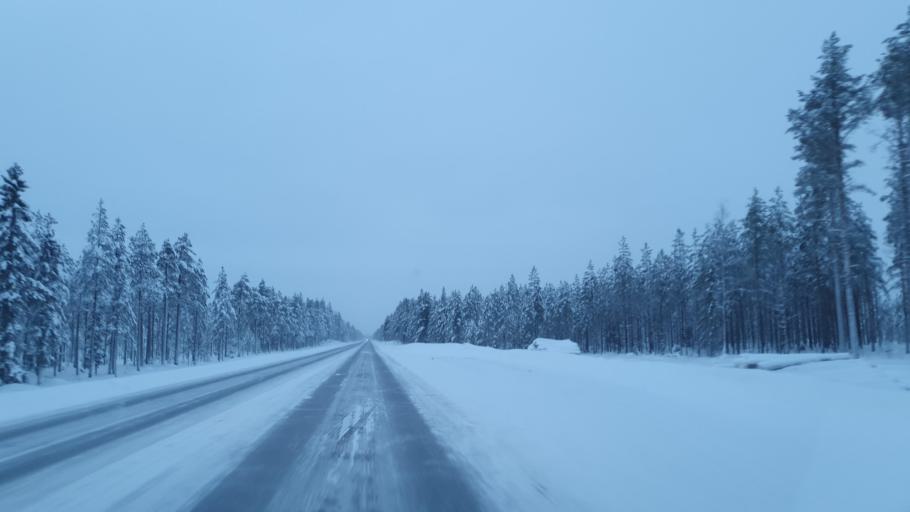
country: FI
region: Kainuu
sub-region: Kajaani
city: Vaala
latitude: 64.5973
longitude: 26.7480
